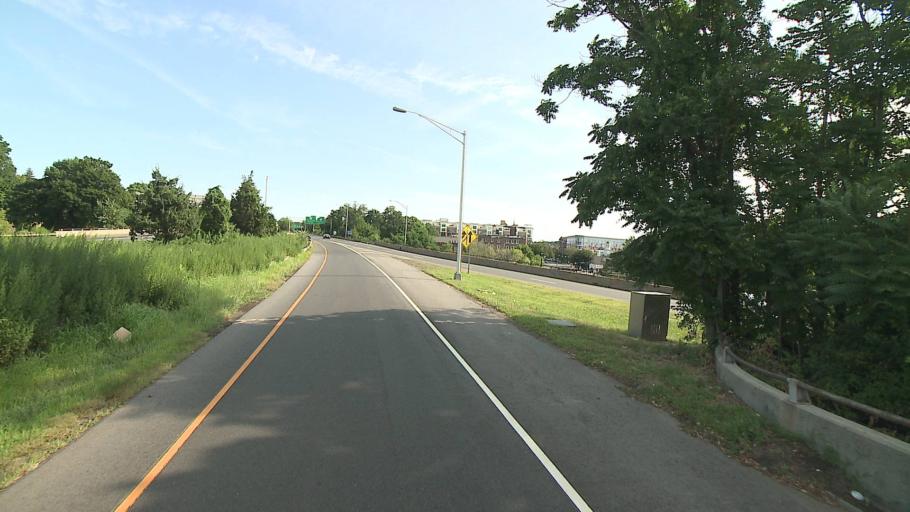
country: US
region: Connecticut
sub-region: Fairfield County
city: Norwalk
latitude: 41.1092
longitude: -73.4190
